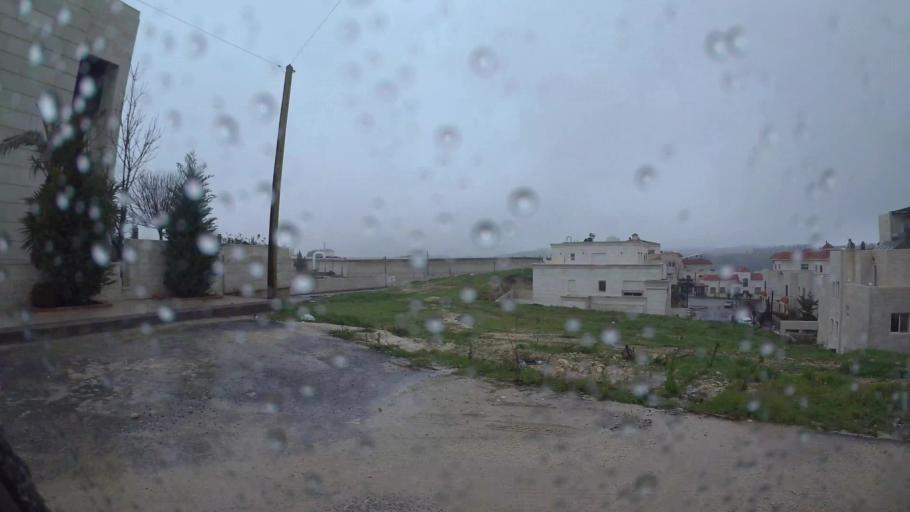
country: JO
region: Amman
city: Al Jubayhah
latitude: 32.0031
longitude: 35.8236
